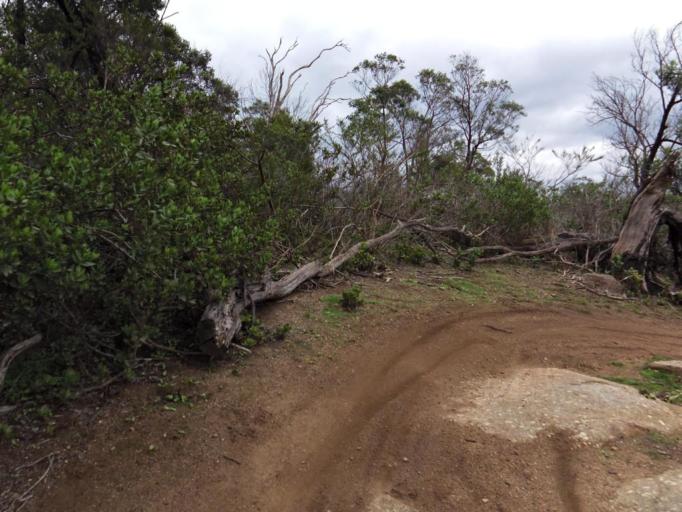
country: AU
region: Victoria
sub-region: Wyndham
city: Little River
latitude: -37.9321
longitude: 144.4335
